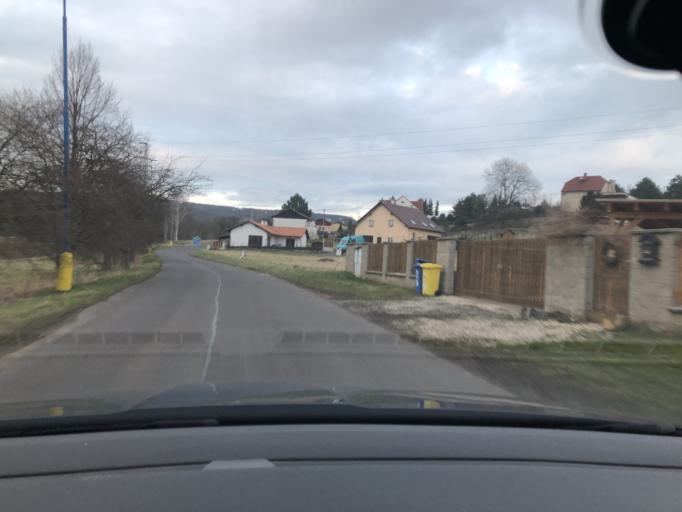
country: CZ
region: Ustecky
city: Rehlovice
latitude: 50.6094
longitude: 13.9562
